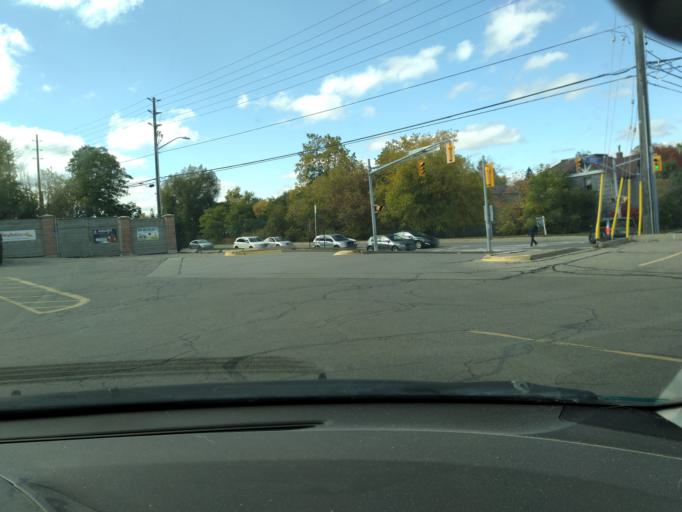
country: CA
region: Ontario
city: Bradford West Gwillimbury
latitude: 44.1125
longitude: -79.5711
